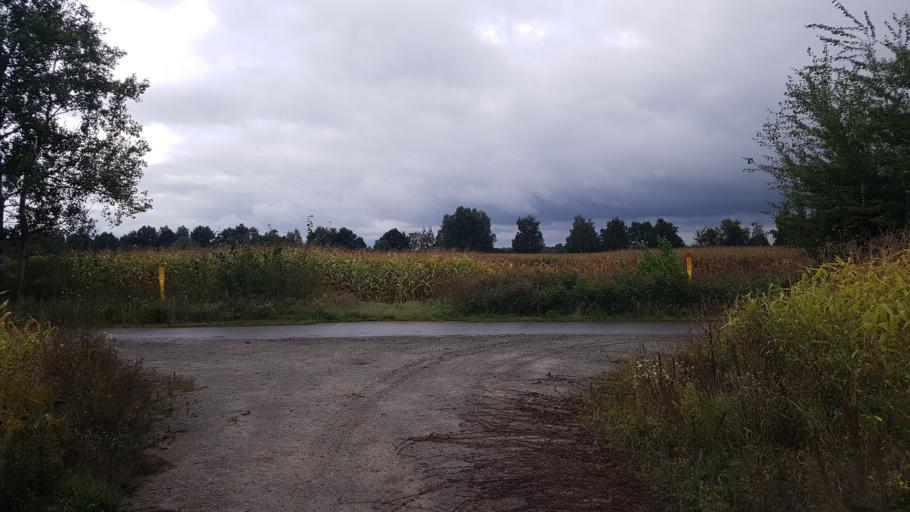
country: DE
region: Brandenburg
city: Tettau
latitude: 51.4624
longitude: 13.7315
